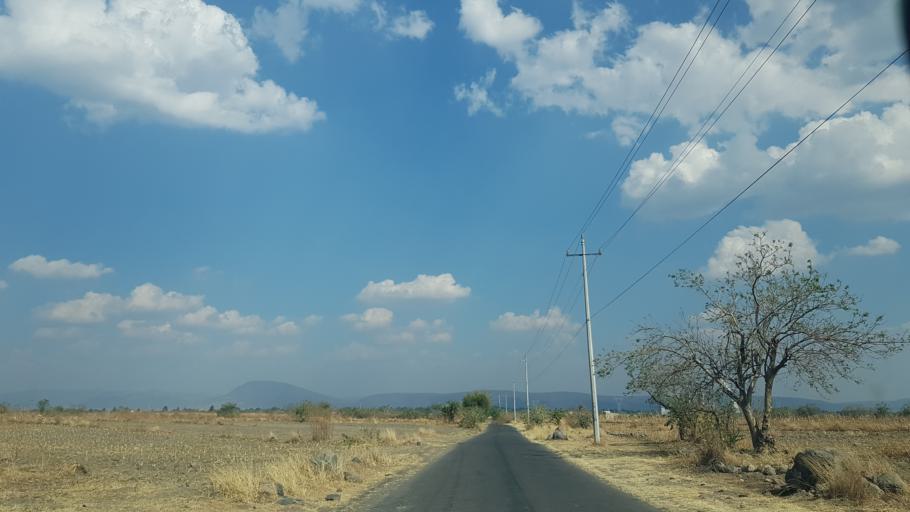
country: MX
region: Puebla
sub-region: Atlixco
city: Colonia Agricola de Ocotepec (Colonia San Jose)
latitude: 18.8904
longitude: -98.5046
